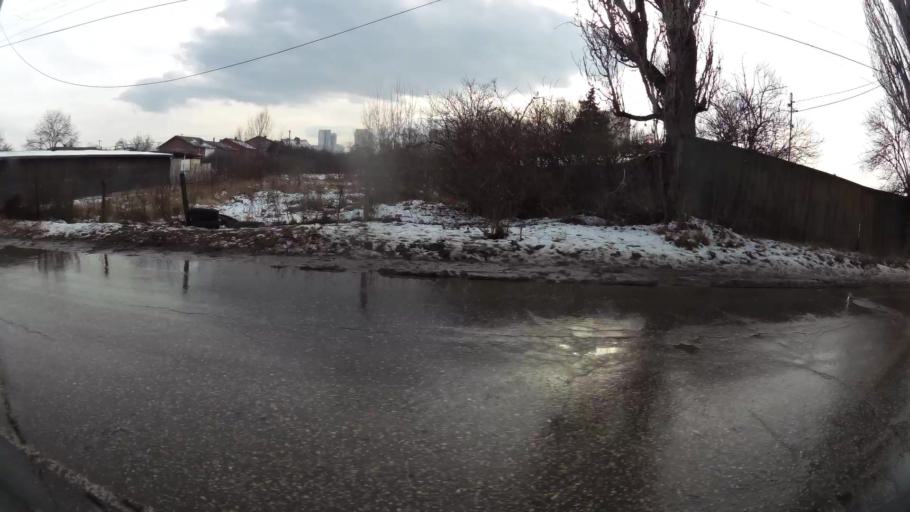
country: BG
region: Sofia-Capital
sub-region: Stolichna Obshtina
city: Sofia
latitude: 42.6943
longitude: 23.3767
